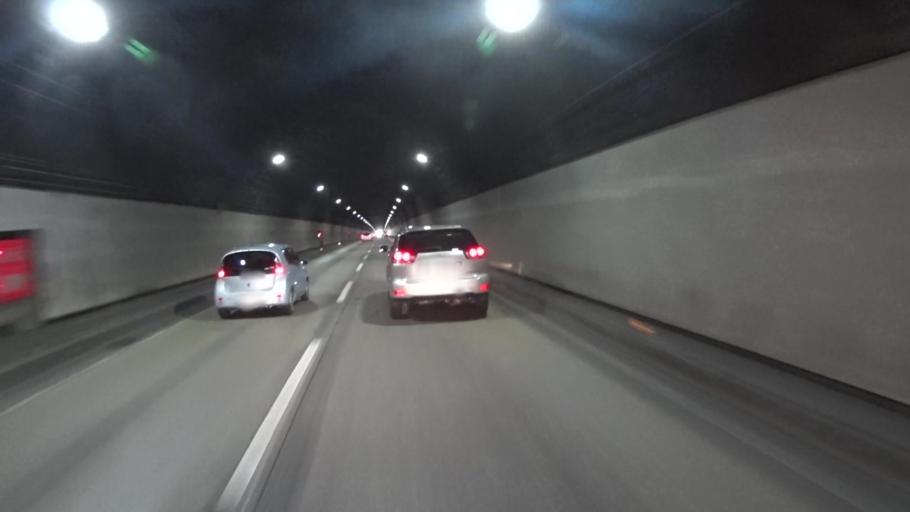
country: JP
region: Shiga Prefecture
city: Otsu-shi
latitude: 35.0126
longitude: 135.8428
